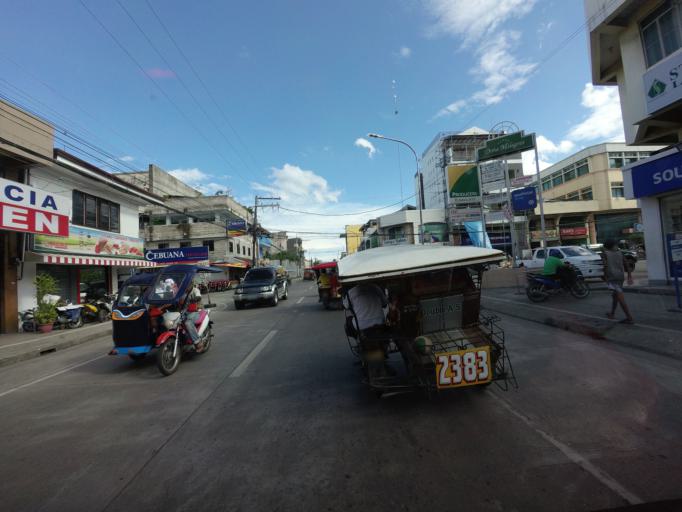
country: PH
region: Central Visayas
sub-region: Province of Negros Oriental
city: Dumaguete
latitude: 9.3039
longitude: 123.3078
